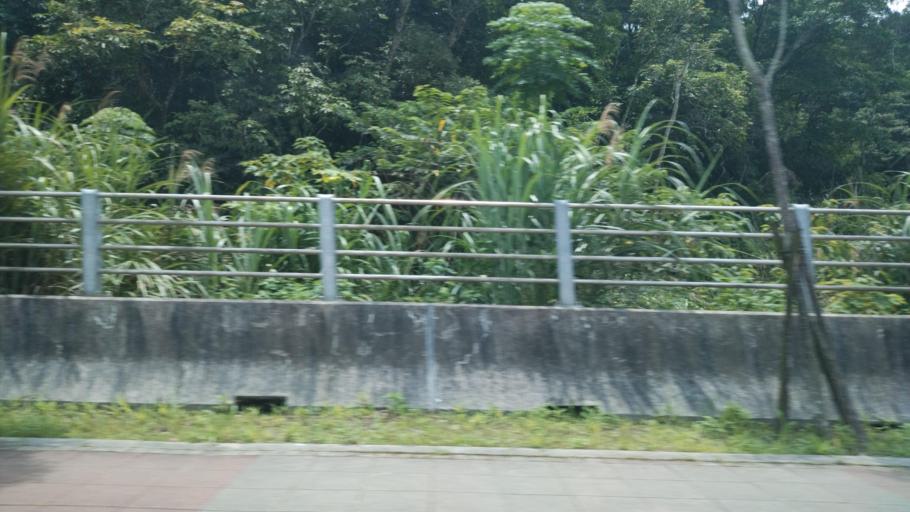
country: TW
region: Taipei
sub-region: Taipei
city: Banqiao
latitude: 24.9462
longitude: 121.4898
